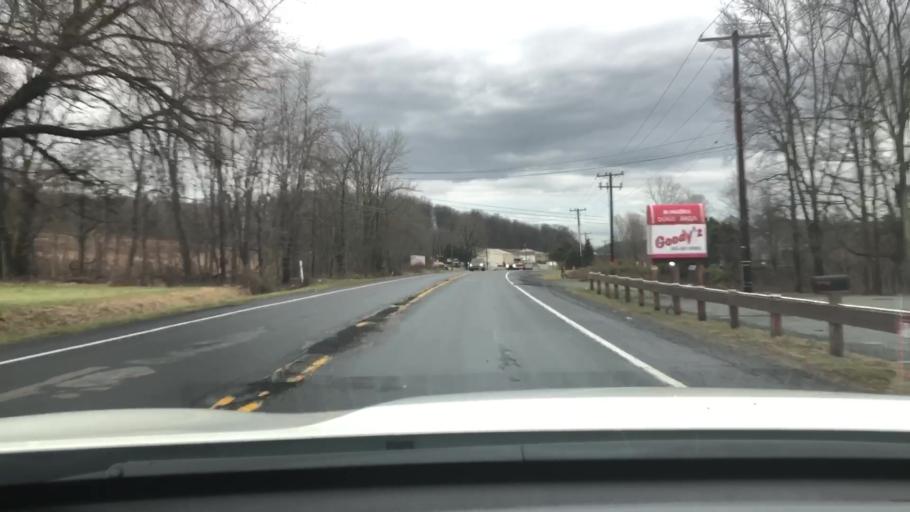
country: US
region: Pennsylvania
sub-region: Berks County
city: Bally
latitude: 40.3758
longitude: -75.6119
